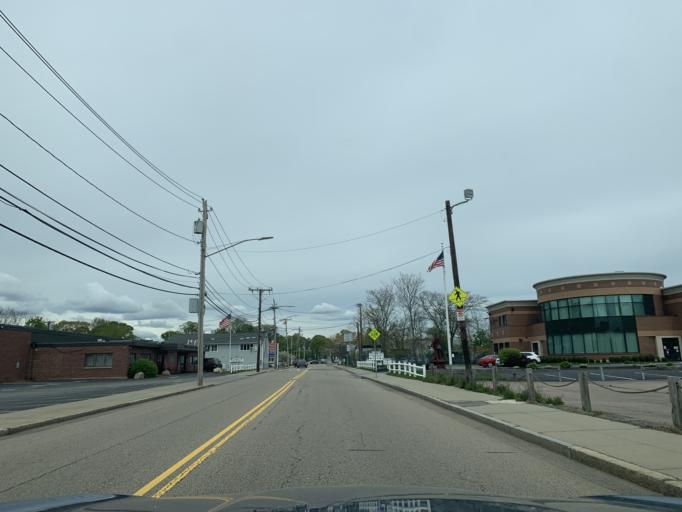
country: US
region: Massachusetts
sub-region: Norfolk County
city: Milton
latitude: 42.2817
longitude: -71.0474
